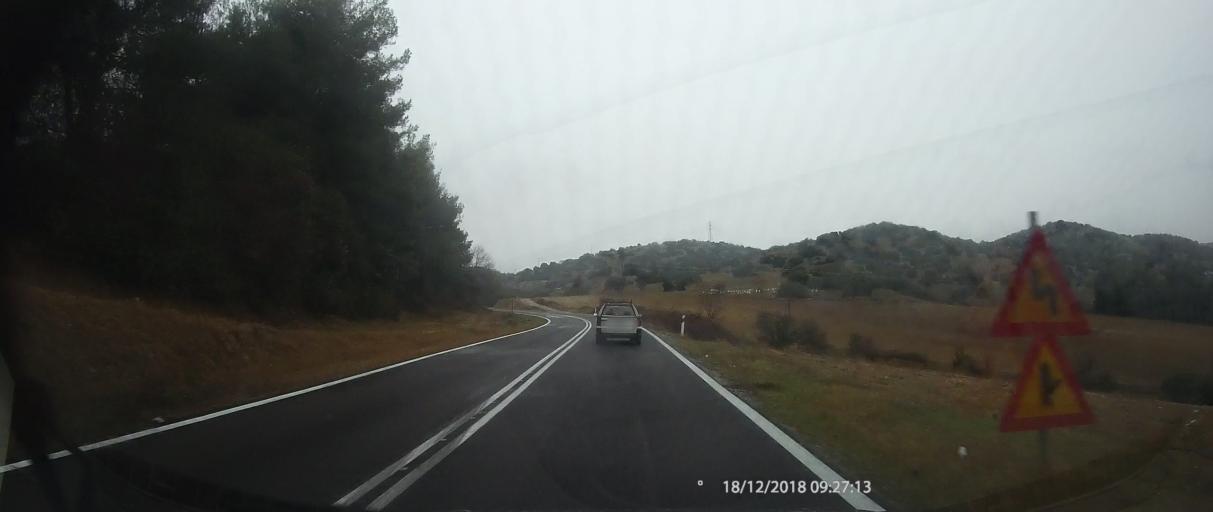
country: GR
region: Thessaly
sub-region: Nomos Larisis
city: Elassona
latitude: 39.9167
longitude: 22.1790
